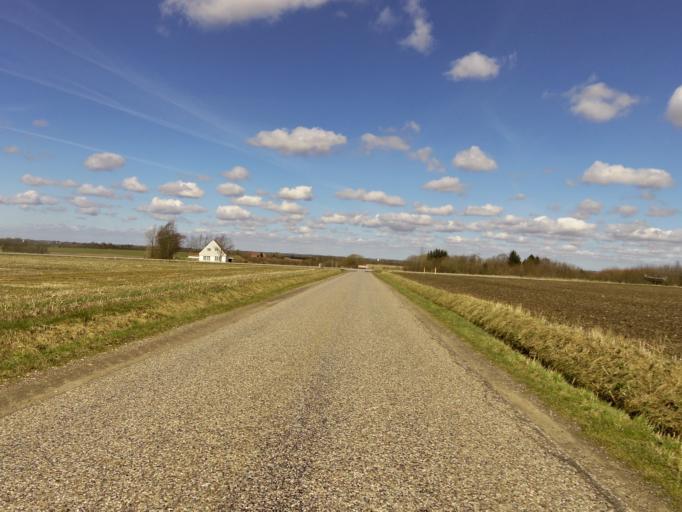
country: DK
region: South Denmark
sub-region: Tonder Kommune
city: Toftlund
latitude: 55.1908
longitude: 9.0955
